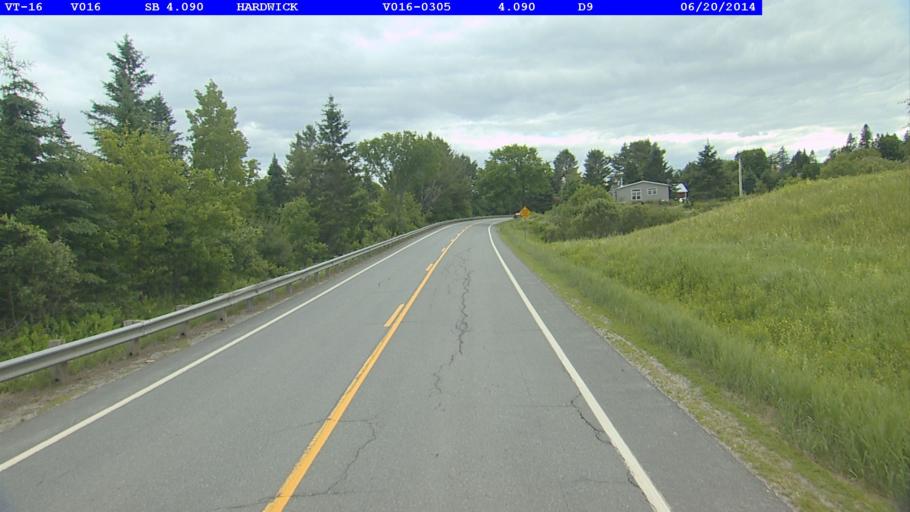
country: US
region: Vermont
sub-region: Caledonia County
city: Hardwick
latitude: 44.5400
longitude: -72.2703
